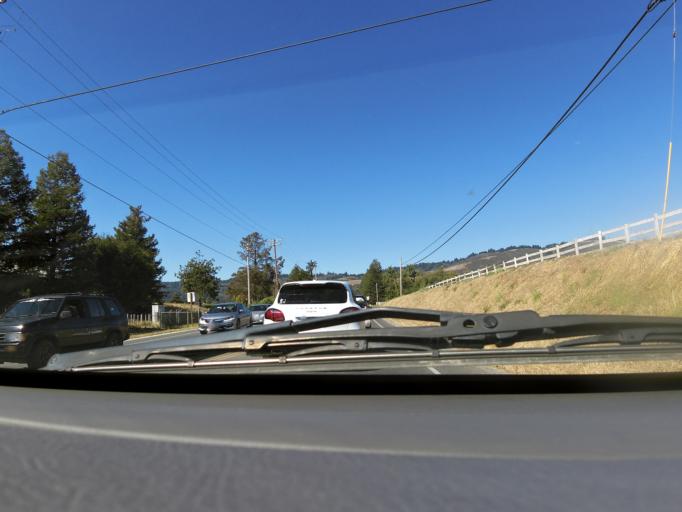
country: US
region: California
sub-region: Santa Cruz County
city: Interlaken
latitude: 36.9500
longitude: -121.7332
